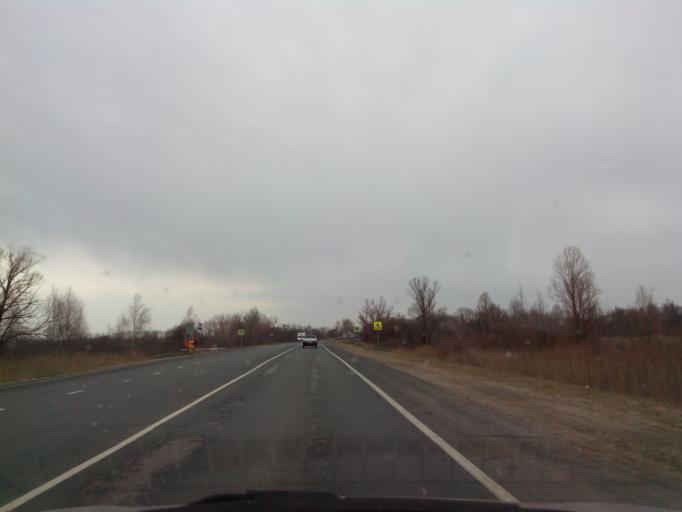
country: RU
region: Tambov
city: Michurinsk
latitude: 53.0814
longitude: 40.4109
